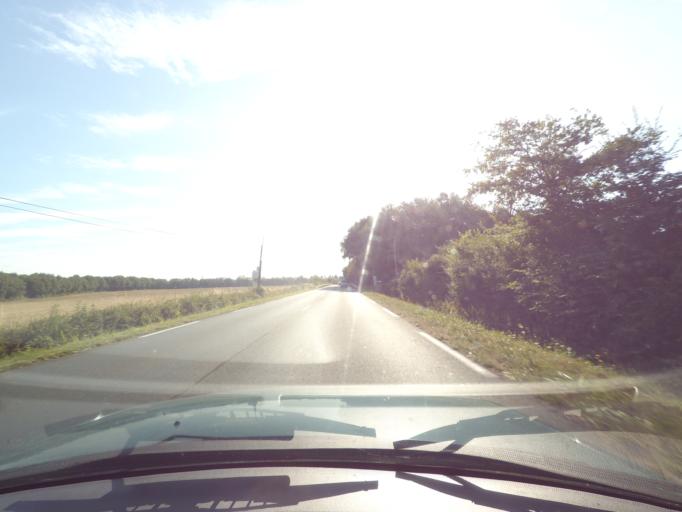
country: FR
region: Poitou-Charentes
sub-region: Departement des Deux-Sevres
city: Thenezay
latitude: 46.6605
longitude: -0.0184
